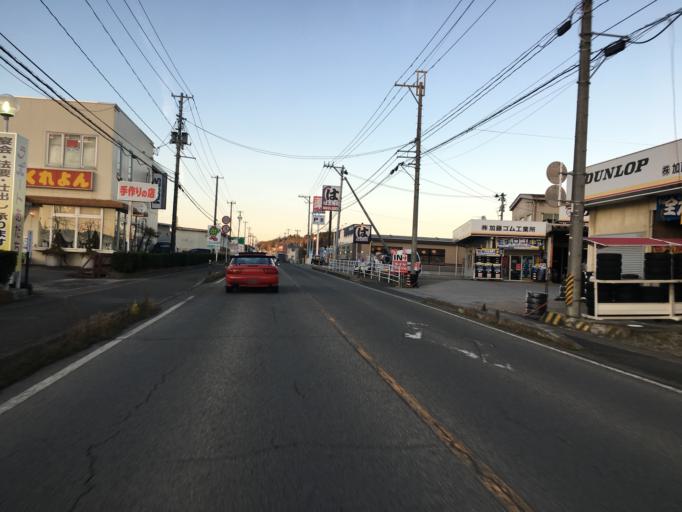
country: JP
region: Fukushima
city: Nihommatsu
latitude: 37.6078
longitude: 140.4606
